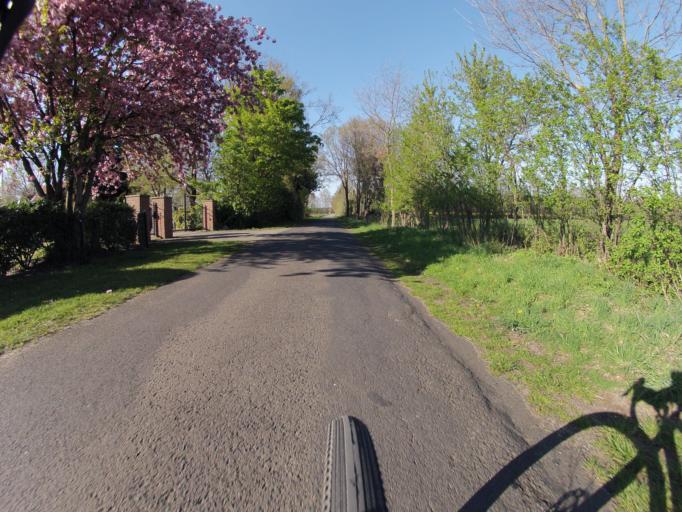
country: DE
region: Lower Saxony
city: Schuttorf
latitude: 52.3482
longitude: 7.2238
